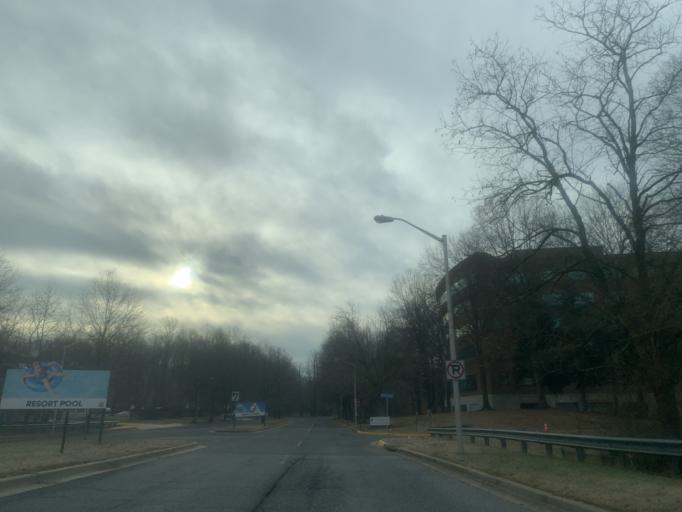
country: US
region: Maryland
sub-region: Prince George's County
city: Forestville
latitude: 38.8286
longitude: -76.8513
